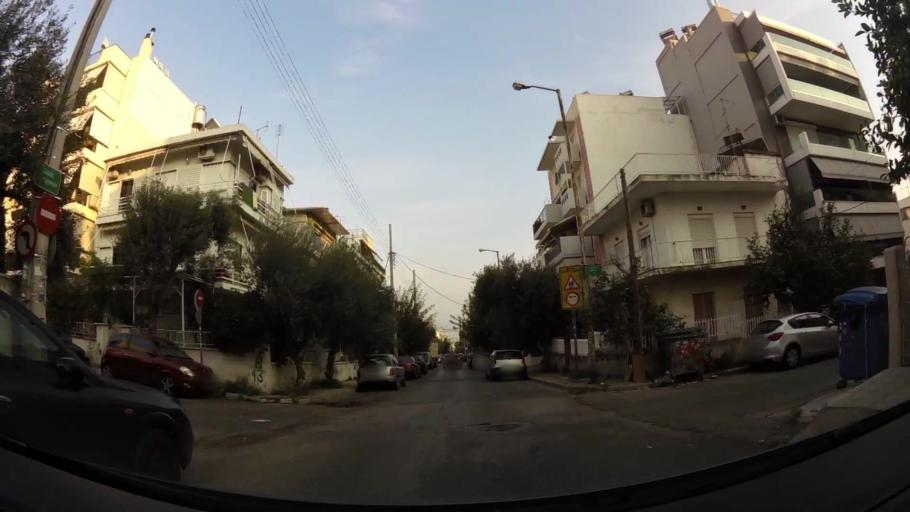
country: GR
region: Attica
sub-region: Nomarchia Athinas
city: Petroupolis
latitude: 38.0420
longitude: 23.6787
